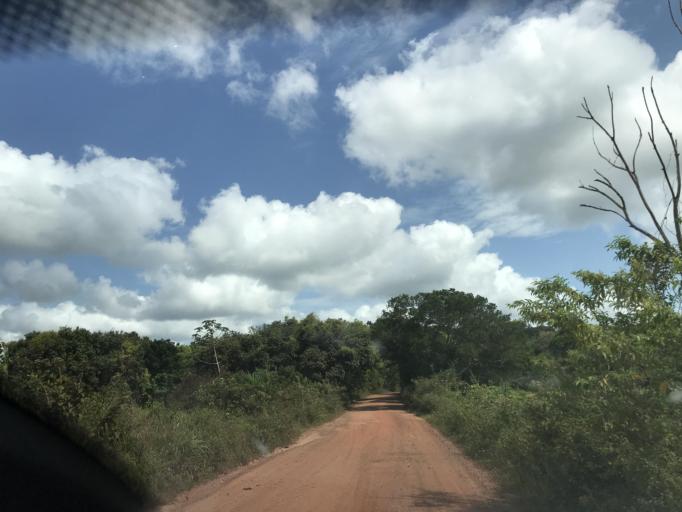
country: BR
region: Bahia
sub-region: Entre Rios
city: Entre Rios
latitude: -12.1626
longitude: -38.0787
